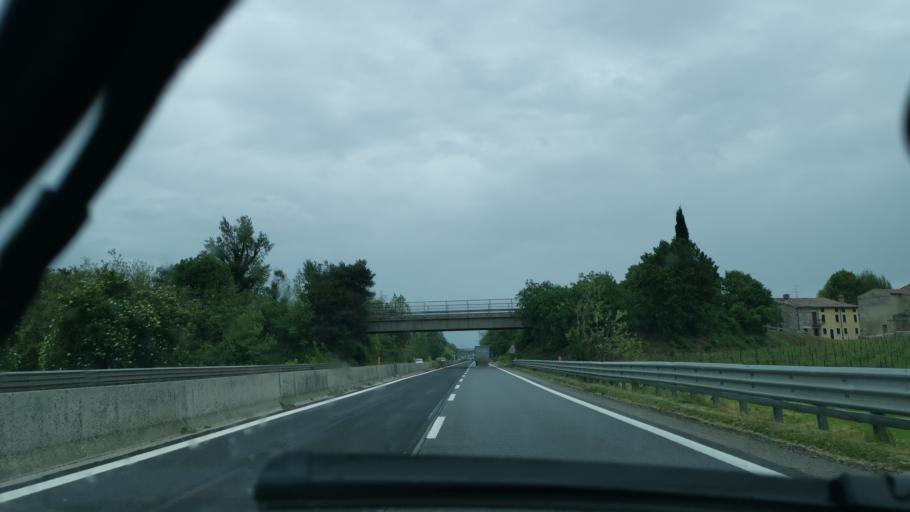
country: IT
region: Veneto
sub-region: Provincia di Verona
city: Cola
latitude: 45.4712
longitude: 10.7616
